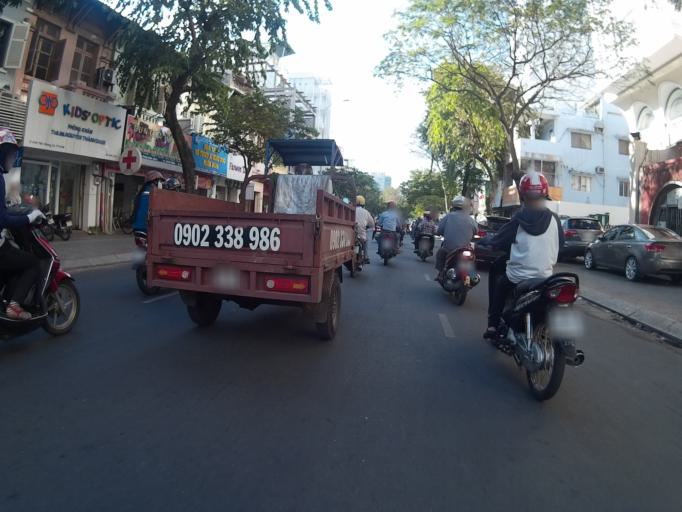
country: VN
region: Ho Chi Minh City
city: Quan Mot
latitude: 10.7887
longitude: 106.6994
